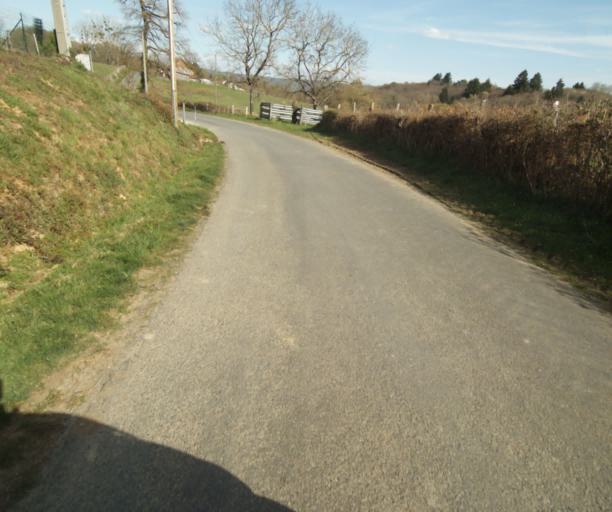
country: FR
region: Limousin
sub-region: Departement de la Correze
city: Seilhac
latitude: 45.3470
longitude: 1.7487
